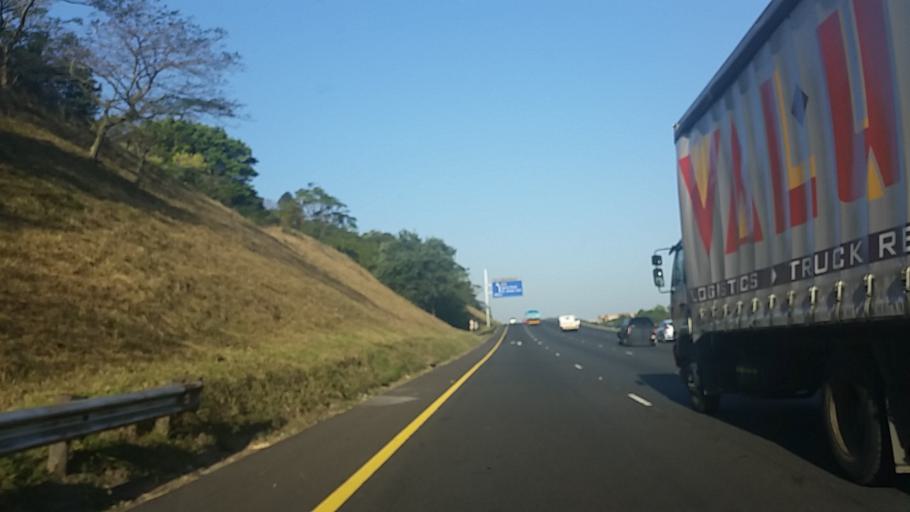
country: ZA
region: KwaZulu-Natal
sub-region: eThekwini Metropolitan Municipality
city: Berea
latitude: -29.8432
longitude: 30.9204
